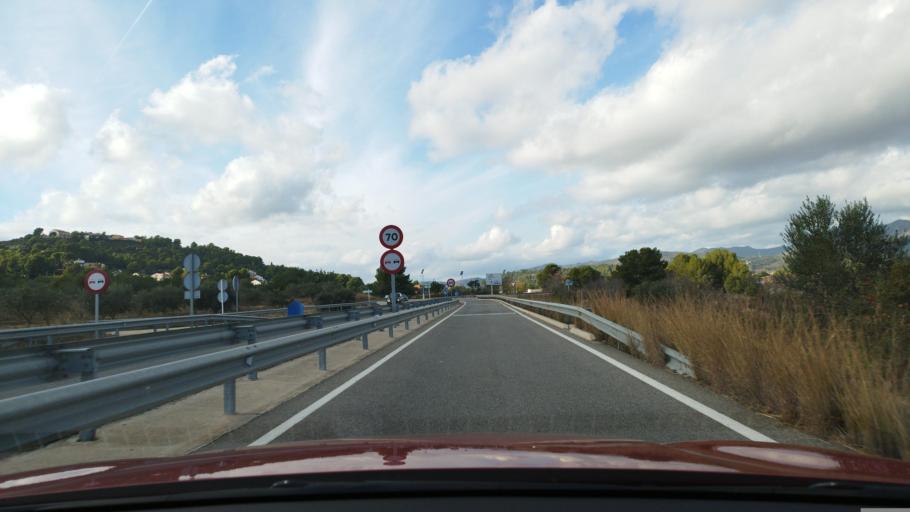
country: ES
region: Catalonia
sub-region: Provincia de Tarragona
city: Albinyana
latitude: 41.2596
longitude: 1.4982
